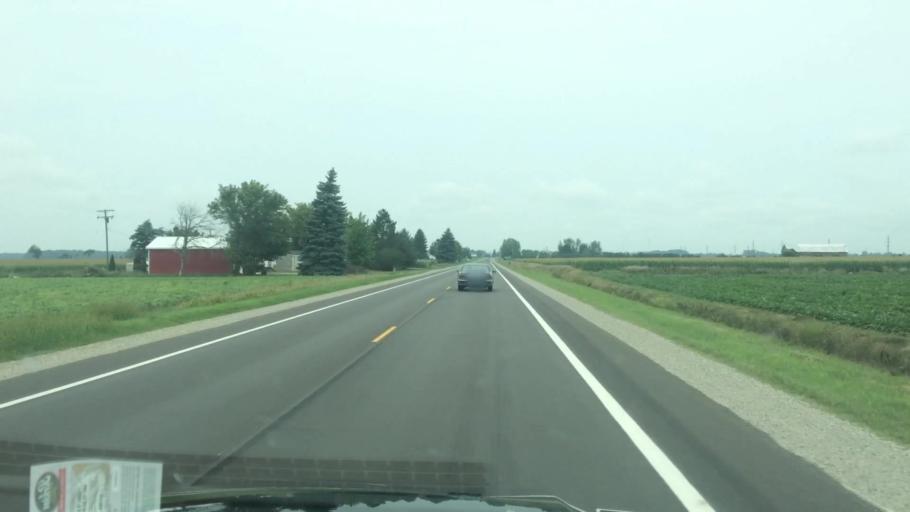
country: US
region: Michigan
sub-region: Huron County
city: Bad Axe
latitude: 43.9918
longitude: -83.0074
